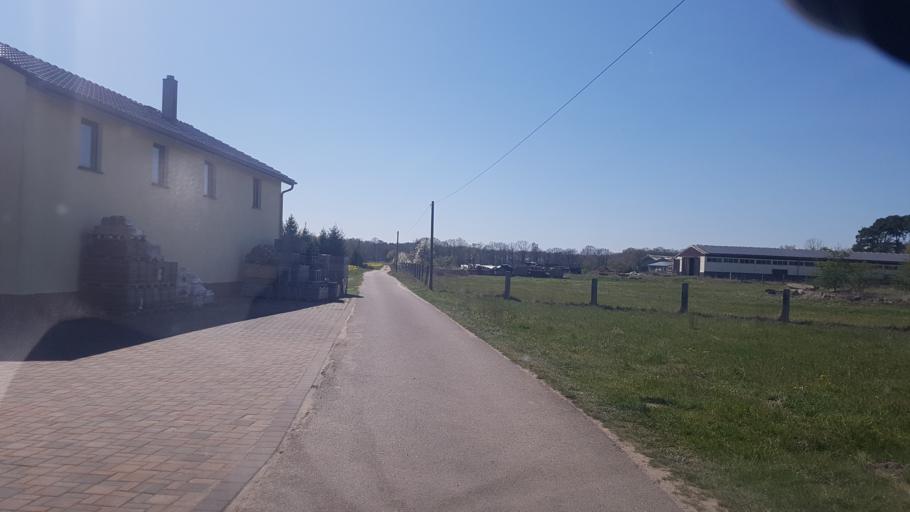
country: DE
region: Brandenburg
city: Sonnewalde
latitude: 51.7136
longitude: 13.6265
